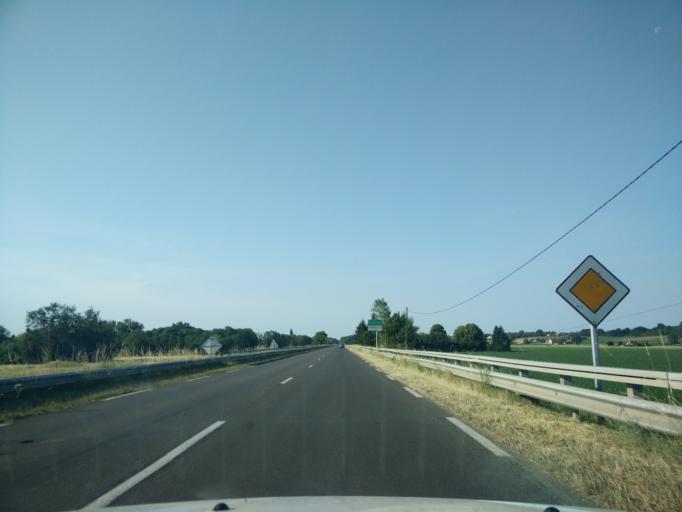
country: FR
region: Auvergne
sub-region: Departement de l'Allier
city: Moulins
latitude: 46.5528
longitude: 3.3208
